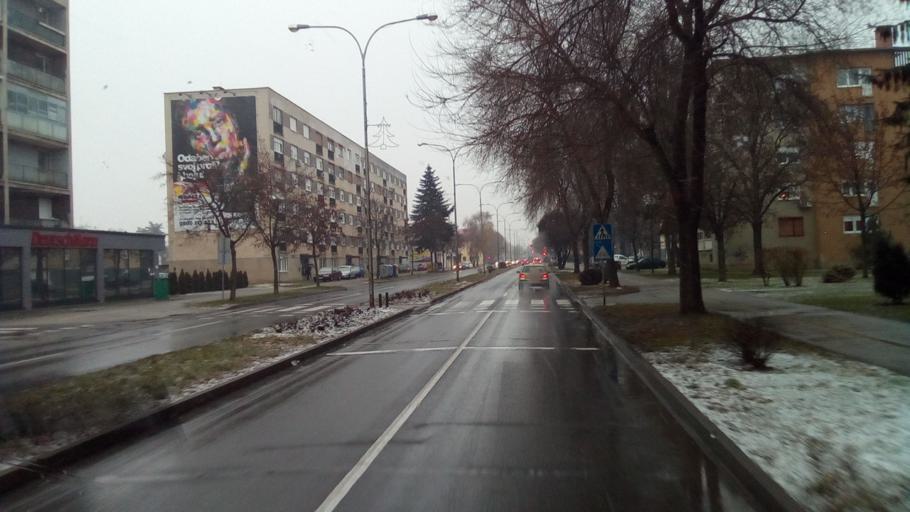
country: HR
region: Varazdinska
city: Varazdin
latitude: 46.3016
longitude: 16.3360
